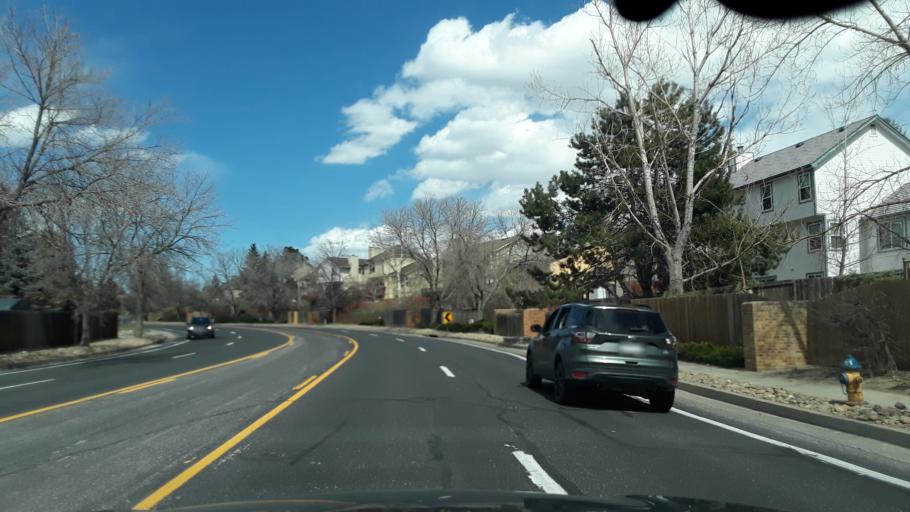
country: US
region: Colorado
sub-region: El Paso County
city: Black Forest
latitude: 38.9444
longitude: -104.7552
